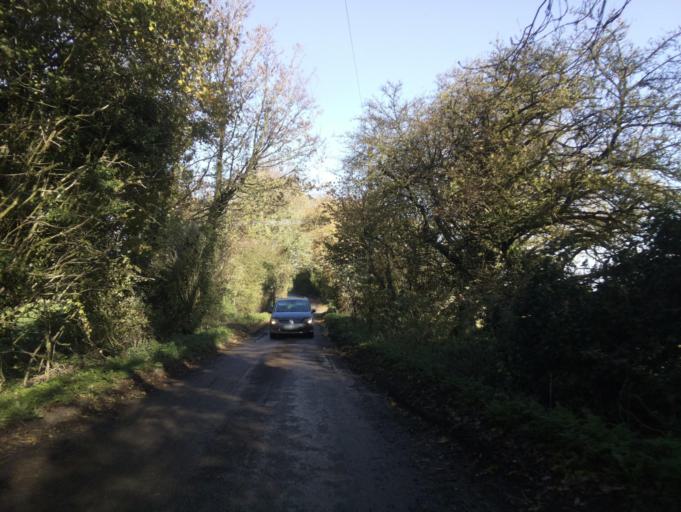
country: GB
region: England
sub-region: Somerset
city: Milborne Port
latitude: 51.0116
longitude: -2.5076
